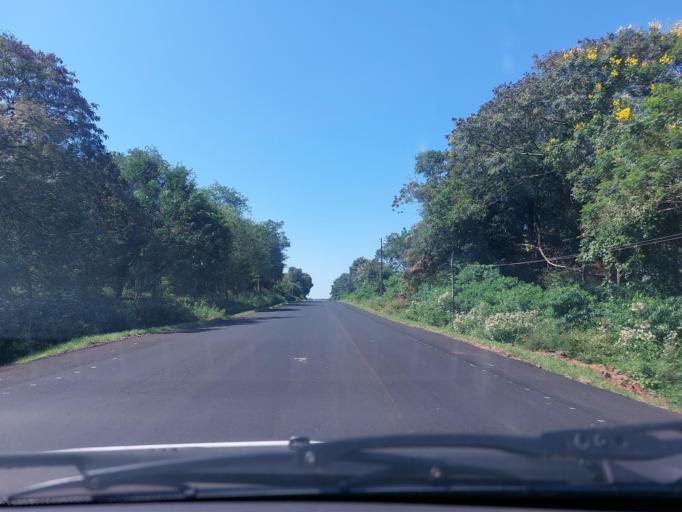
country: PY
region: San Pedro
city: Guayaybi
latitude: -24.5504
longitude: -56.4975
